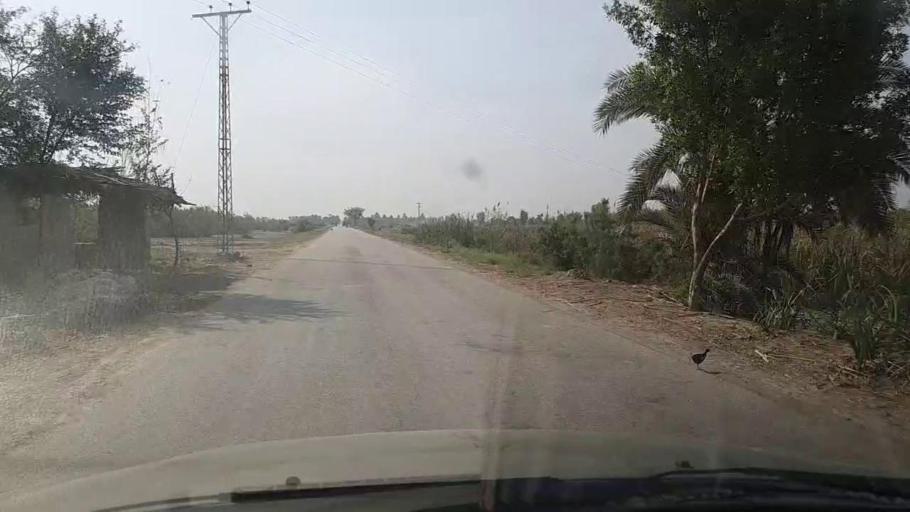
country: PK
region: Sindh
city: Gambat
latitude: 27.4756
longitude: 68.4719
